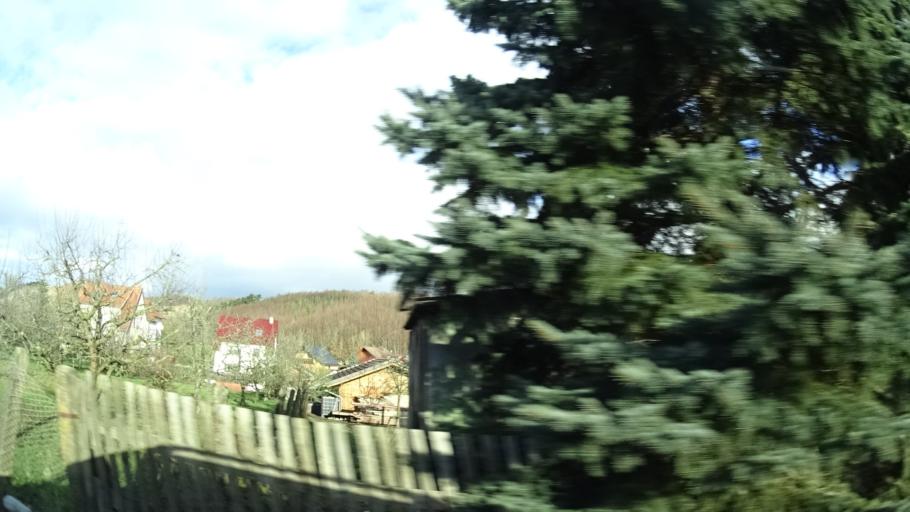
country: DE
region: Thuringia
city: Rossdorf
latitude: 50.7045
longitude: 10.2082
